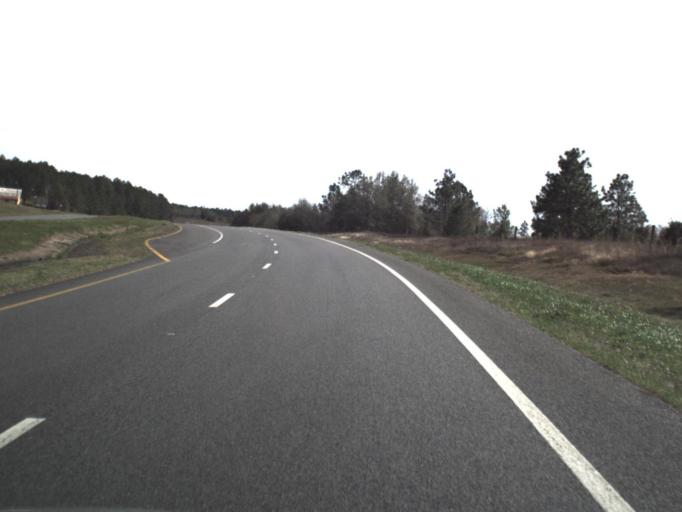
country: US
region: Florida
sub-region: Bay County
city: Youngstown
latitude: 30.5830
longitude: -85.3937
